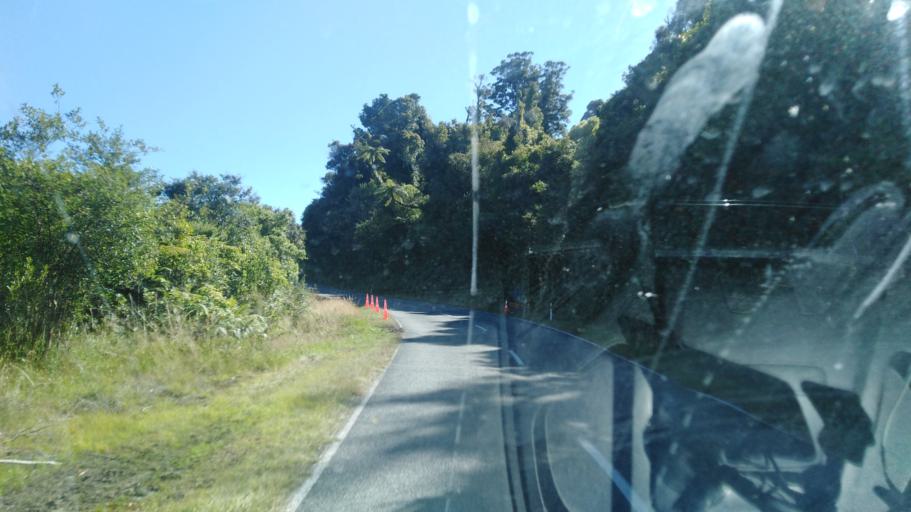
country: NZ
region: West Coast
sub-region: Buller District
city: Westport
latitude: -41.5284
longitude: 172.0085
